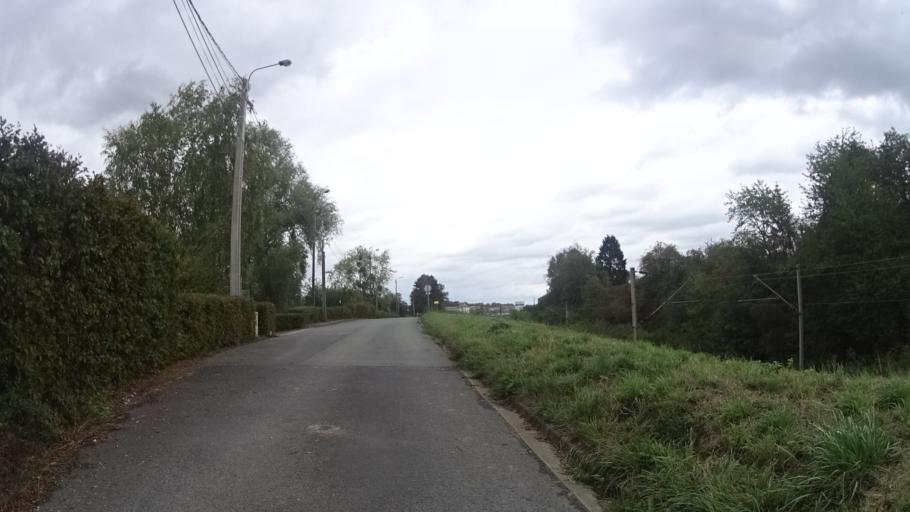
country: FR
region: Nord-Pas-de-Calais
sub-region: Departement du Nord
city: Hautmont
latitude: 50.2409
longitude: 3.8954
